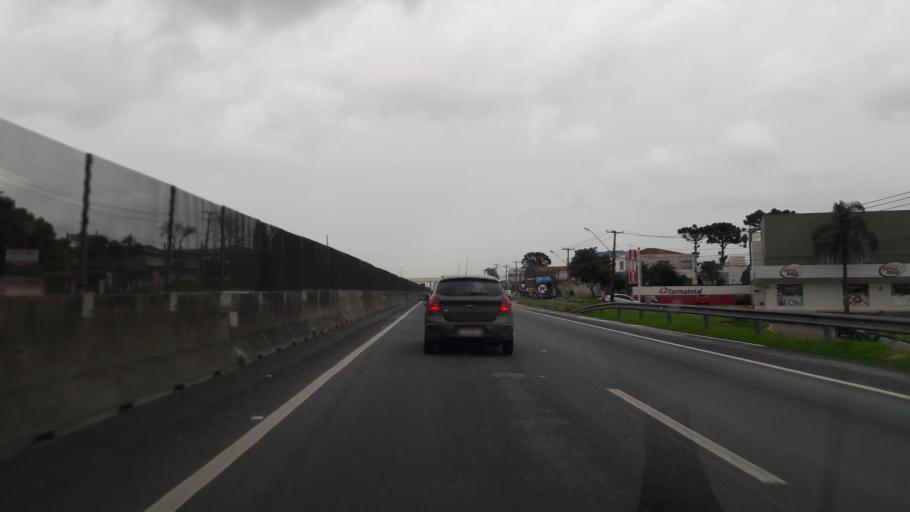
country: BR
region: Parana
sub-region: Pinhais
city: Pinhais
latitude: -25.4721
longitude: -49.2116
